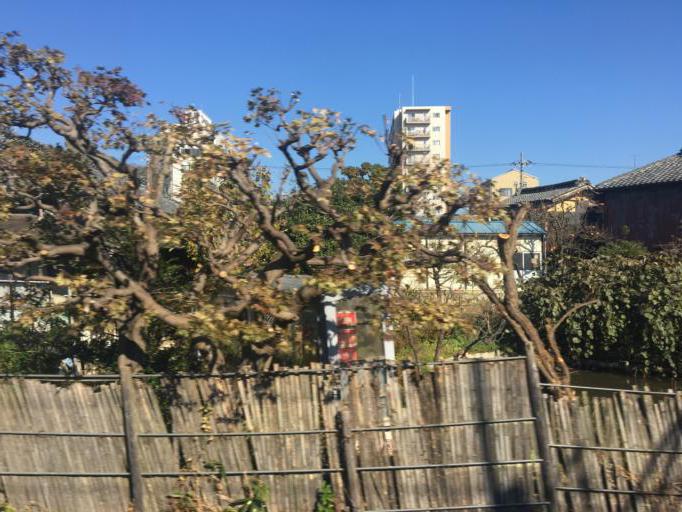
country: JP
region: Tochigi
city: Ashikaga
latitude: 36.3352
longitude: 139.4457
